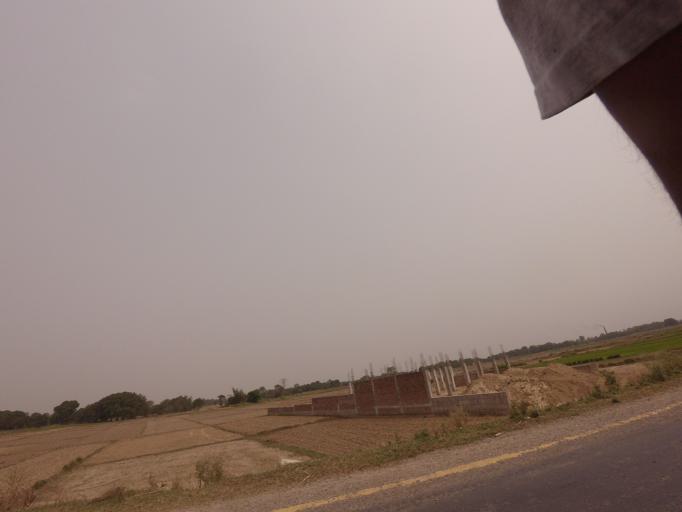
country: IN
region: Uttar Pradesh
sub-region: Maharajganj
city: Nautanwa
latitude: 27.4984
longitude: 83.3297
